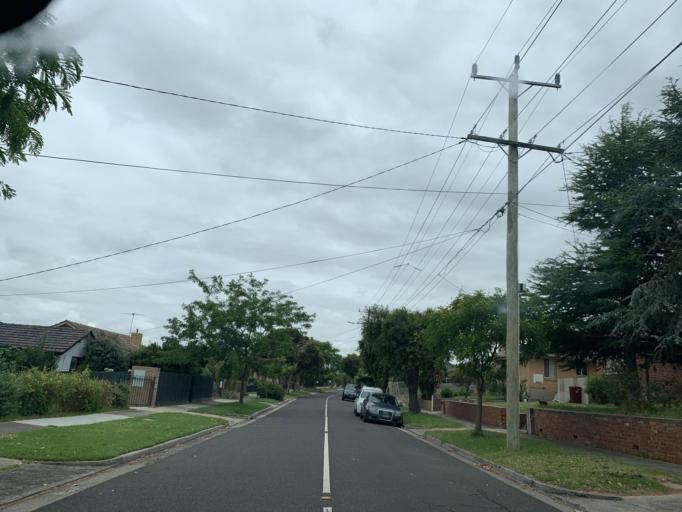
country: AU
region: Victoria
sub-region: Hume
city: Jacana
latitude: -37.6894
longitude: 144.9091
